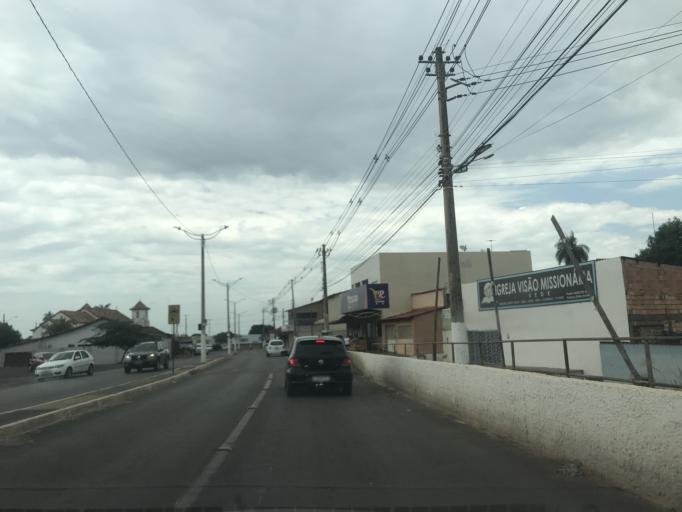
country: BR
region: Goias
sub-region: Luziania
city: Luziania
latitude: -16.2460
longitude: -47.9474
